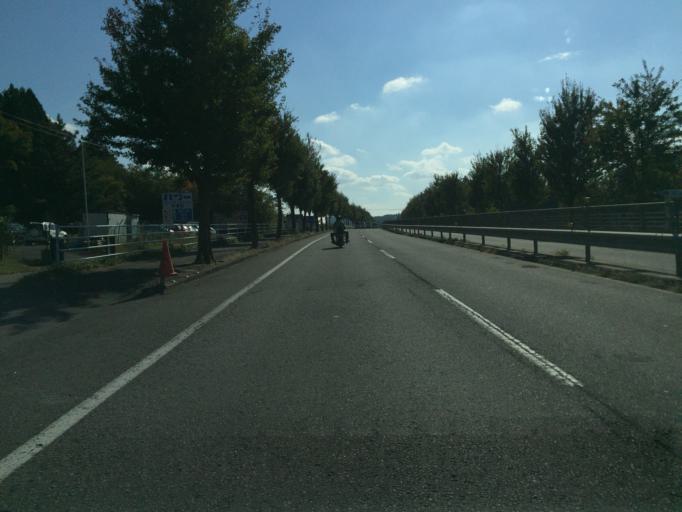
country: JP
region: Fukushima
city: Nihommatsu
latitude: 37.6428
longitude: 140.4860
